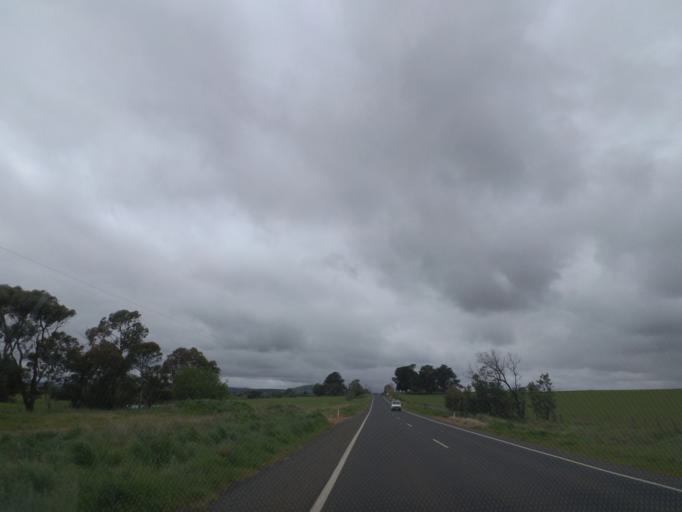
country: AU
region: Victoria
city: Brown Hill
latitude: -37.4105
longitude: 143.9765
